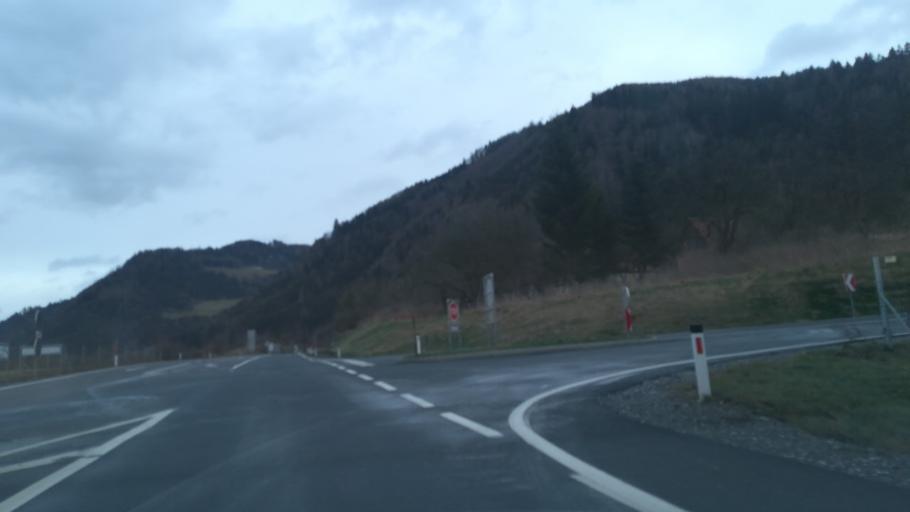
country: AT
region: Styria
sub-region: Politischer Bezirk Murtal
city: Sankt Georgen ob Judenburg
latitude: 47.2037
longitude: 14.5097
